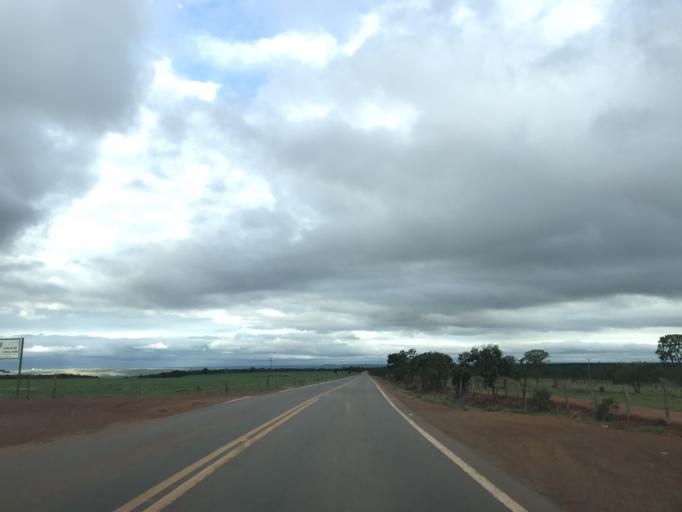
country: BR
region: Goias
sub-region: Luziania
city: Luziania
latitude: -16.3883
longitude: -48.1518
